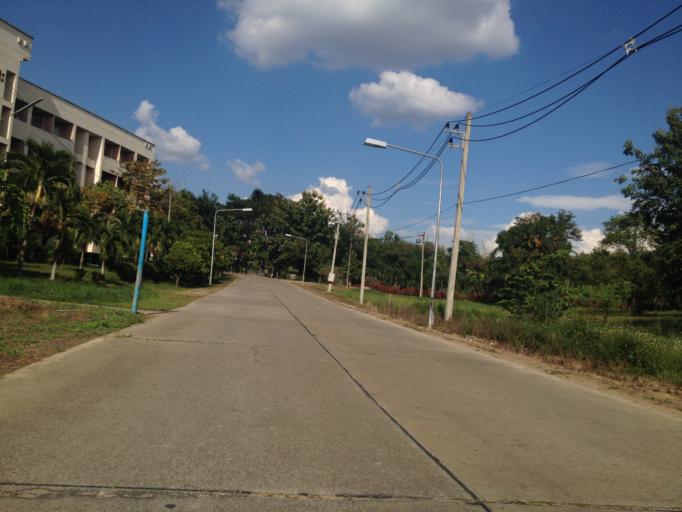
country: TH
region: Chiang Mai
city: Chiang Mai
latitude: 18.7638
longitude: 98.9390
